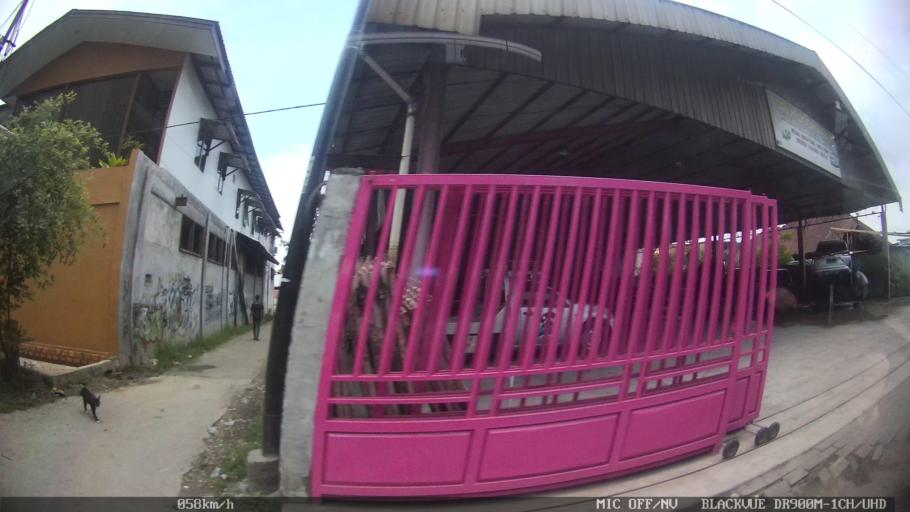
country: ID
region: North Sumatra
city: Labuhan Deli
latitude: 3.6897
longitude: 98.6694
